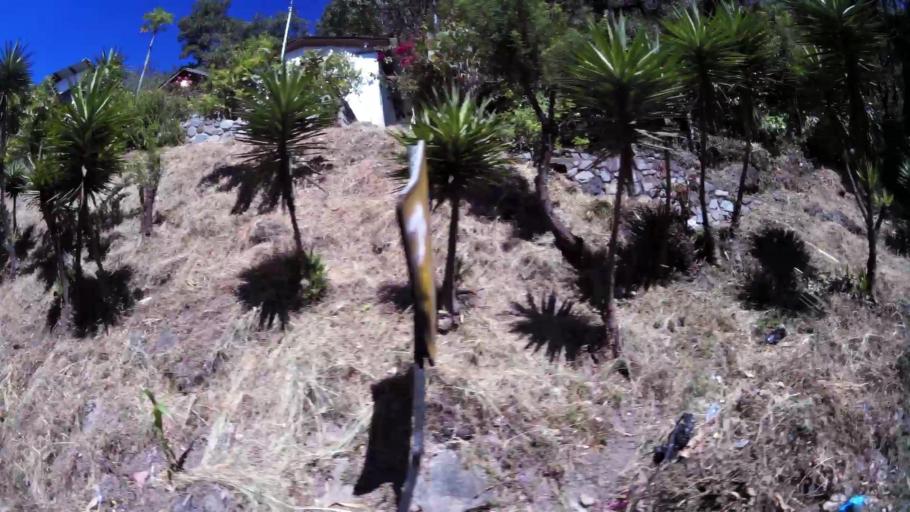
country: GT
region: Solola
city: Solola
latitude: 14.7537
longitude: -91.1715
